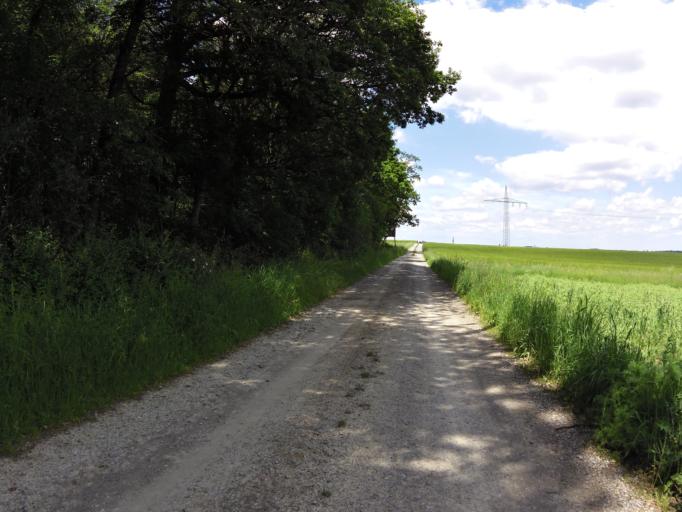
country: DE
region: Bavaria
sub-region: Regierungsbezirk Unterfranken
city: Theilheim
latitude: 49.7316
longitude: 10.0659
